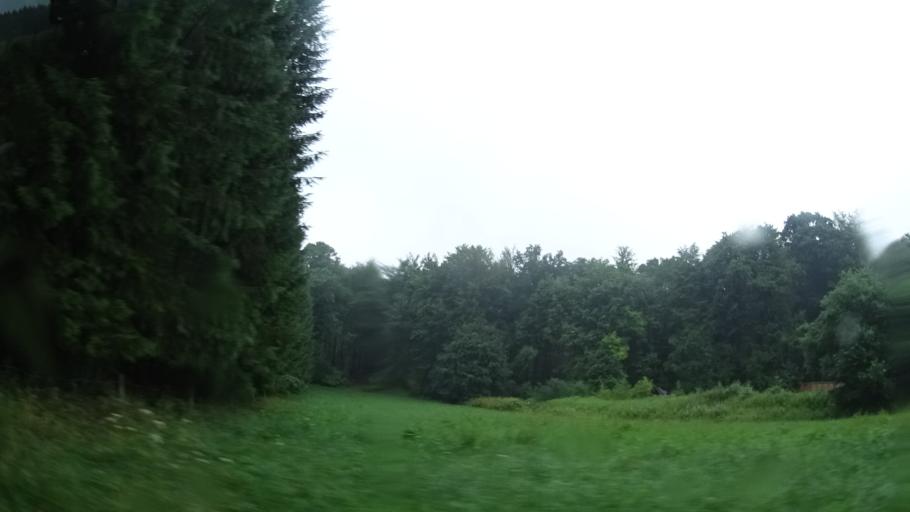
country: BE
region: Wallonia
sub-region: Province de Namur
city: Bievre
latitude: 49.9531
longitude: 5.0475
